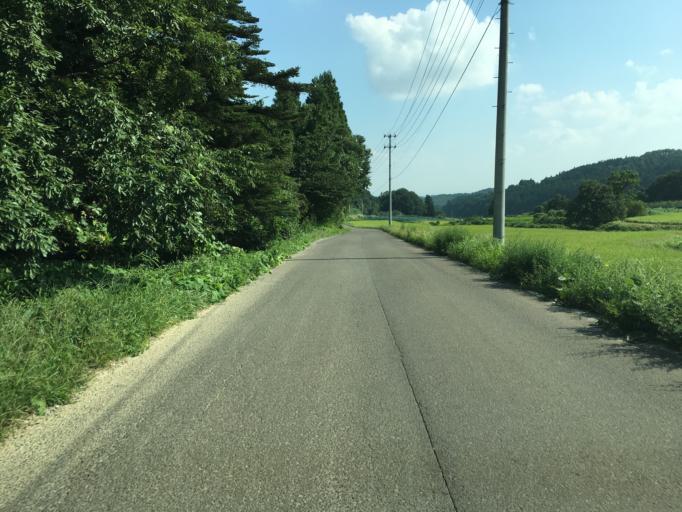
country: JP
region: Fukushima
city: Nihommatsu
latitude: 37.6130
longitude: 140.3932
